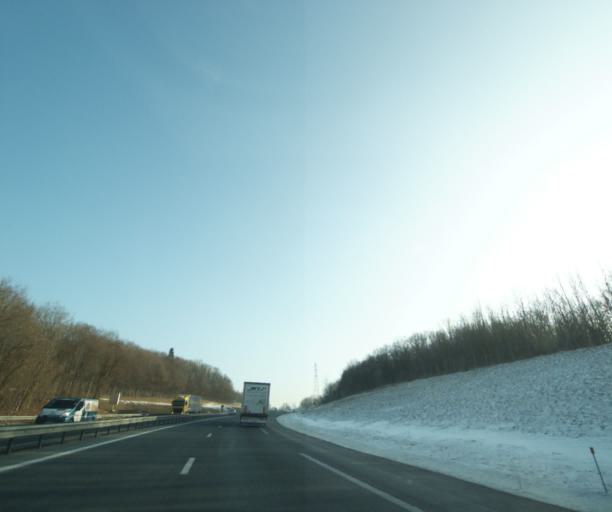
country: FR
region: Rhone-Alpes
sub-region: Departement de l'Ain
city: Bellegarde-sur-Valserine
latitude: 46.0921
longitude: 5.8308
